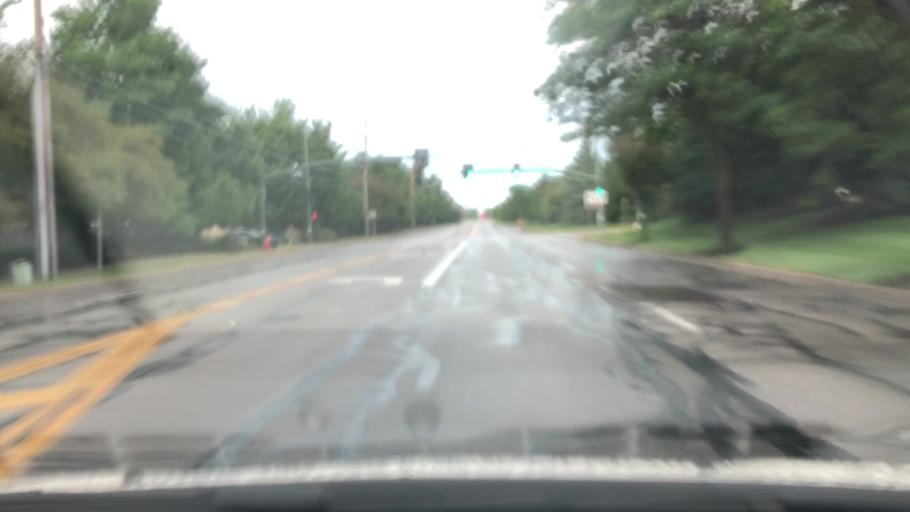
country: US
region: Ohio
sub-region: Franklin County
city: Westerville
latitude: 40.1317
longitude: -82.8937
